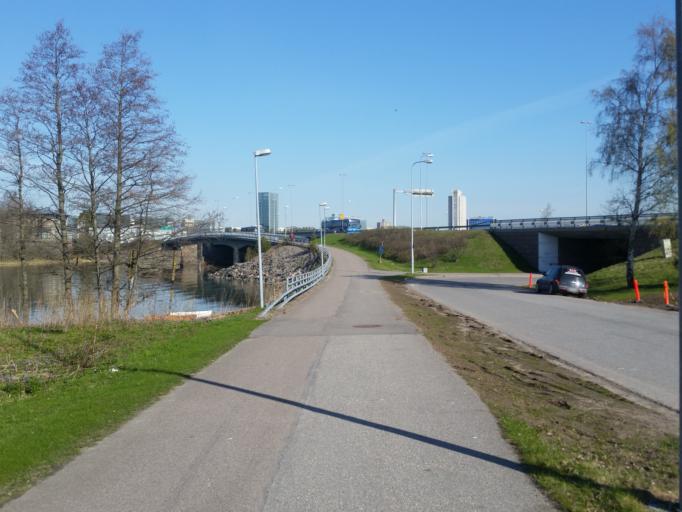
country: FI
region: Uusimaa
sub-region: Helsinki
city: Otaniemi
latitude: 60.1657
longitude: 24.8406
